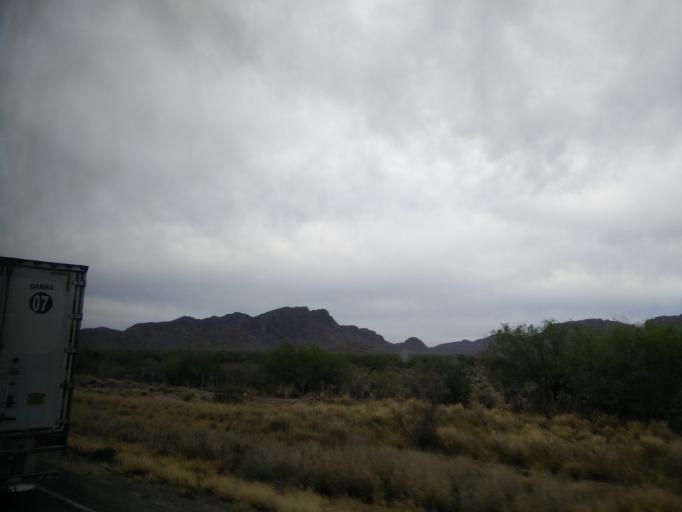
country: MX
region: Sonora
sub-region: Hermosillo
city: Miguel Aleman (La Doce)
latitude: 28.5767
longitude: -111.0298
